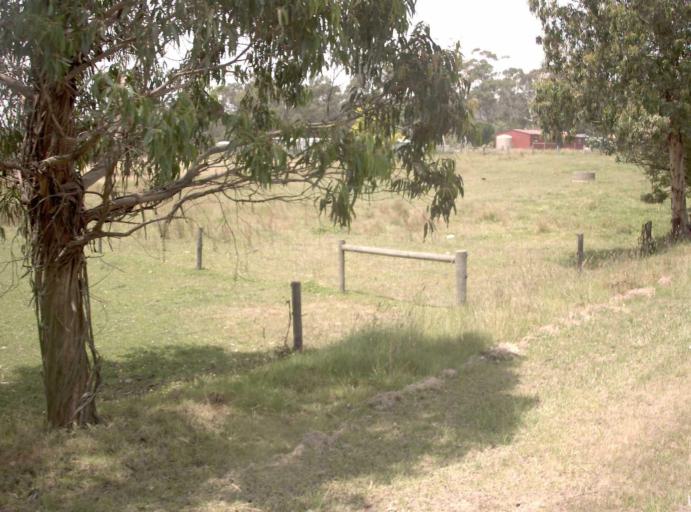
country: AU
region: Victoria
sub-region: Latrobe
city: Traralgon
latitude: -38.3747
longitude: 146.7543
